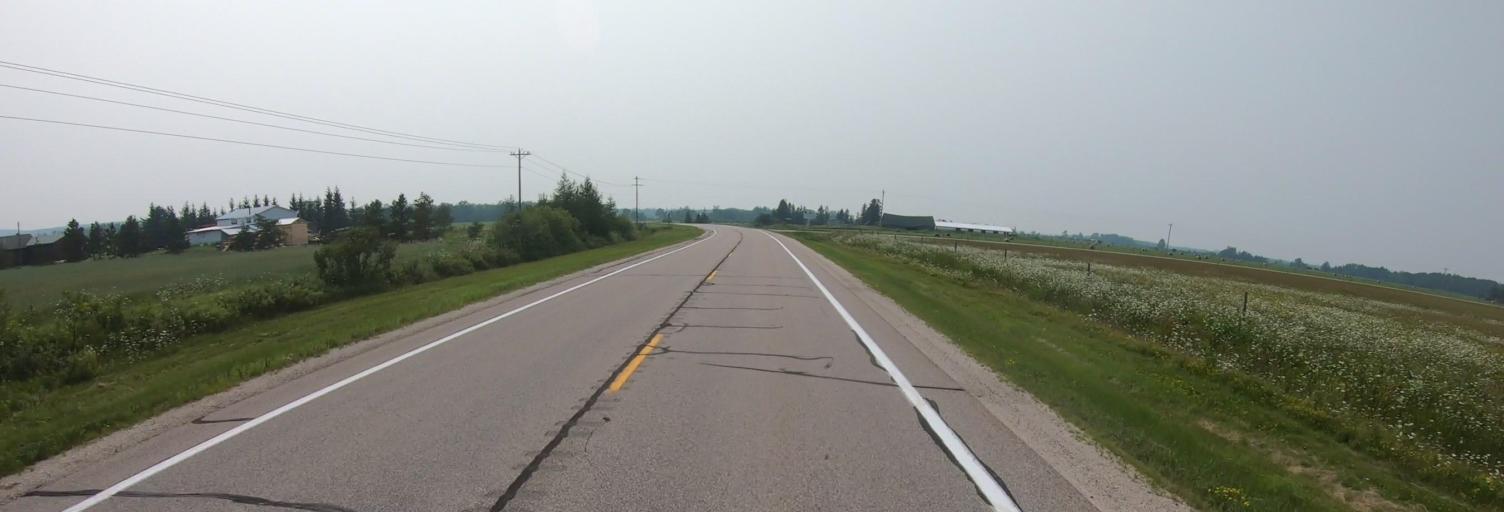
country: US
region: Michigan
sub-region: Chippewa County
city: Sault Ste. Marie
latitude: 46.1290
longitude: -84.3200
